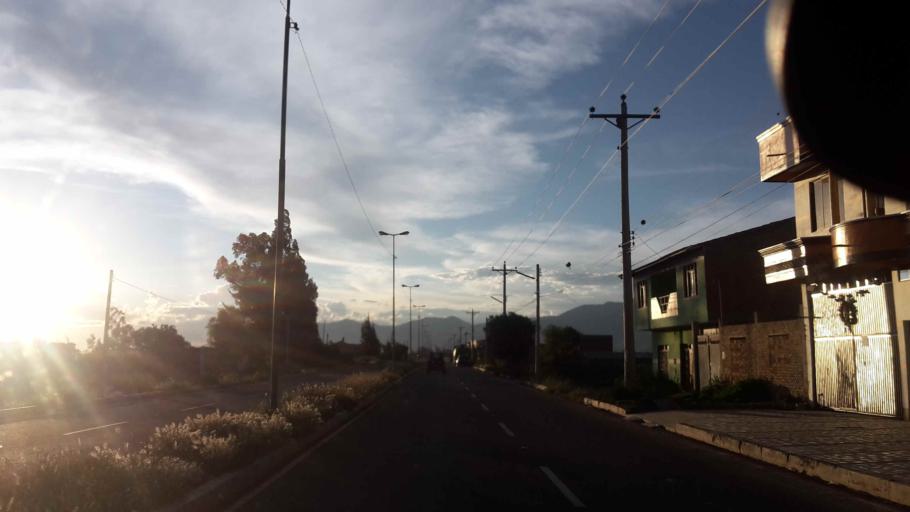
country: BO
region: Cochabamba
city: Punata
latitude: -17.5568
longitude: -65.8083
